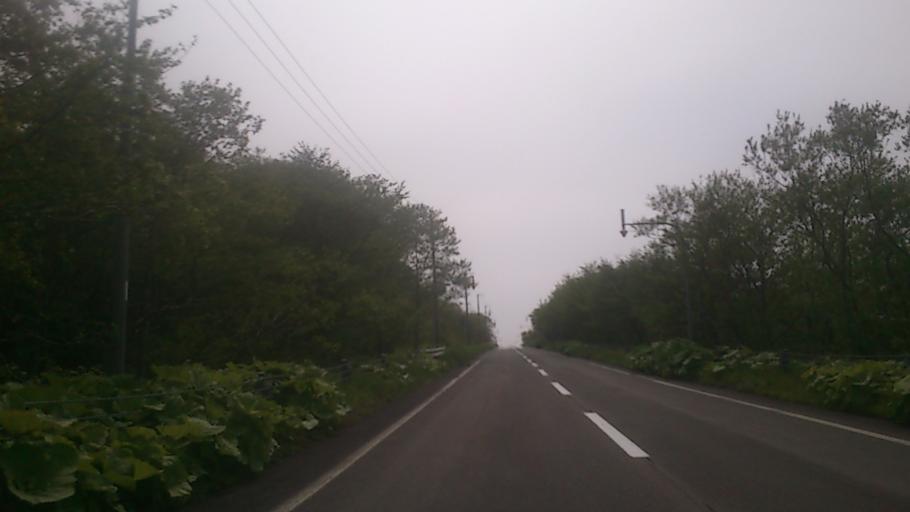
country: JP
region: Hokkaido
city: Nemuro
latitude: 43.1768
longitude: 145.3226
